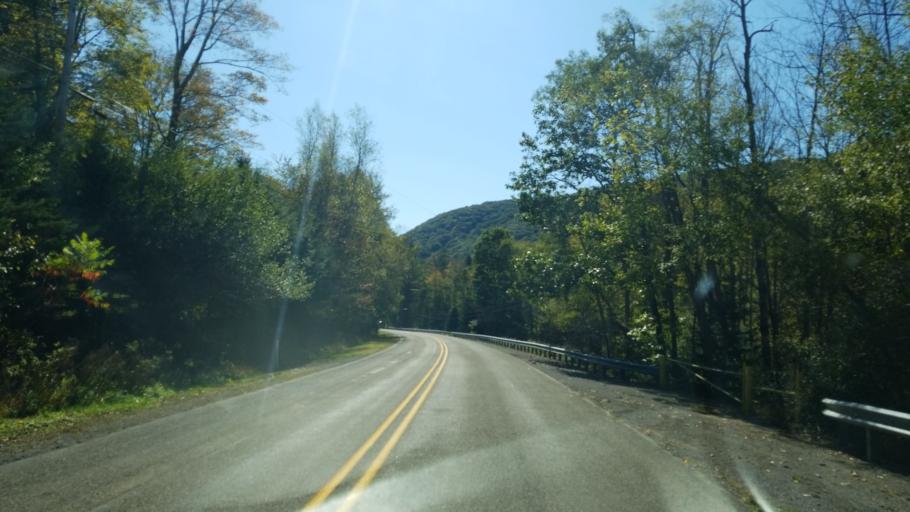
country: US
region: Pennsylvania
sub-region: Elk County
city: Saint Marys
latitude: 41.2817
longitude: -78.3963
